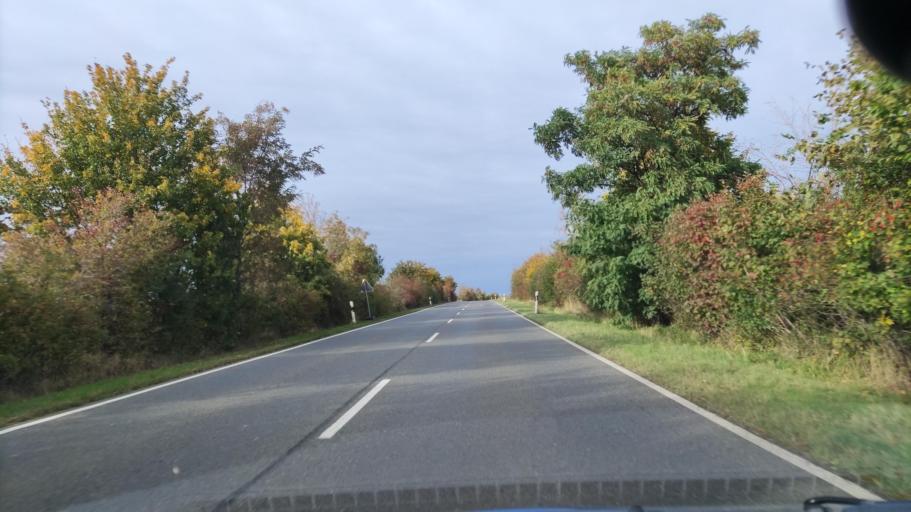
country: DE
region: Saxony-Anhalt
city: Darlingerode
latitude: 51.8542
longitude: 10.7552
